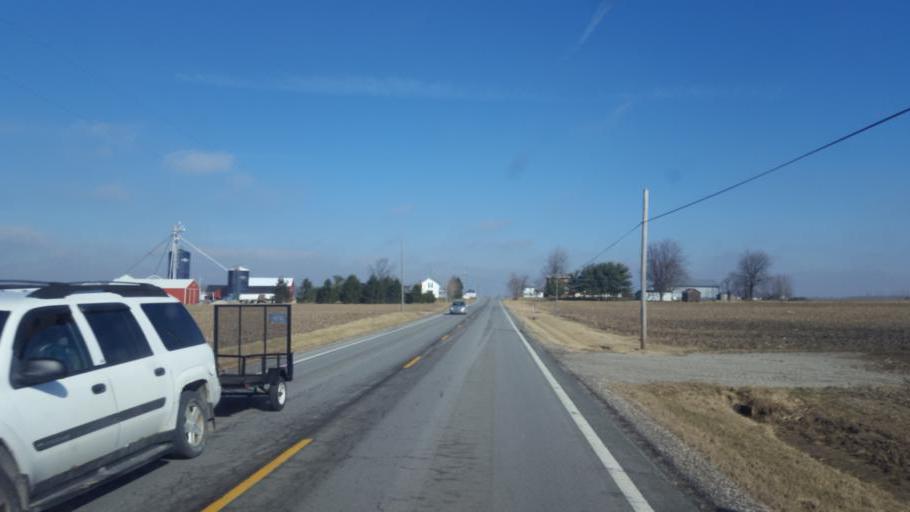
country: US
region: Ohio
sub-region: Crawford County
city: Bucyrus
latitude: 40.9153
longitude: -82.9531
